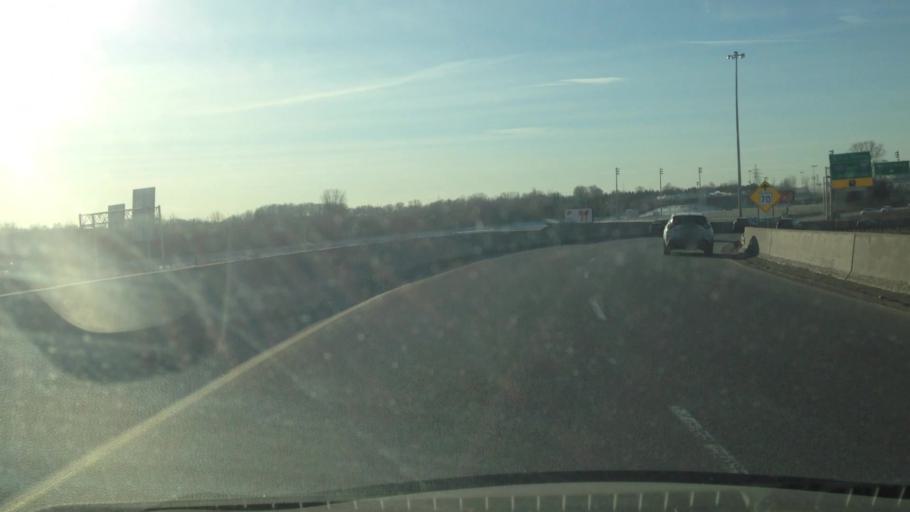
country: CA
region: Quebec
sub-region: Laurentides
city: Boisbriand
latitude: 45.6263
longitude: -73.8433
